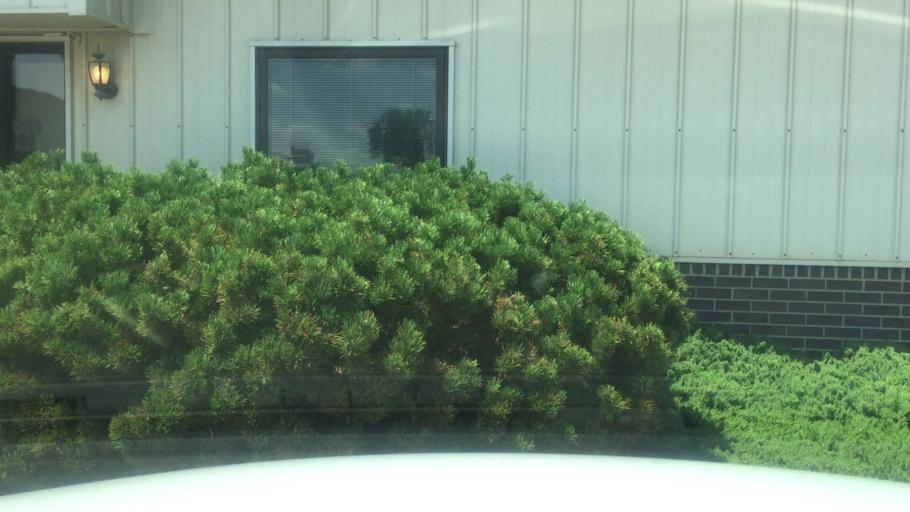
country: US
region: Kansas
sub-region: Brown County
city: Horton
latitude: 39.6573
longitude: -95.5293
